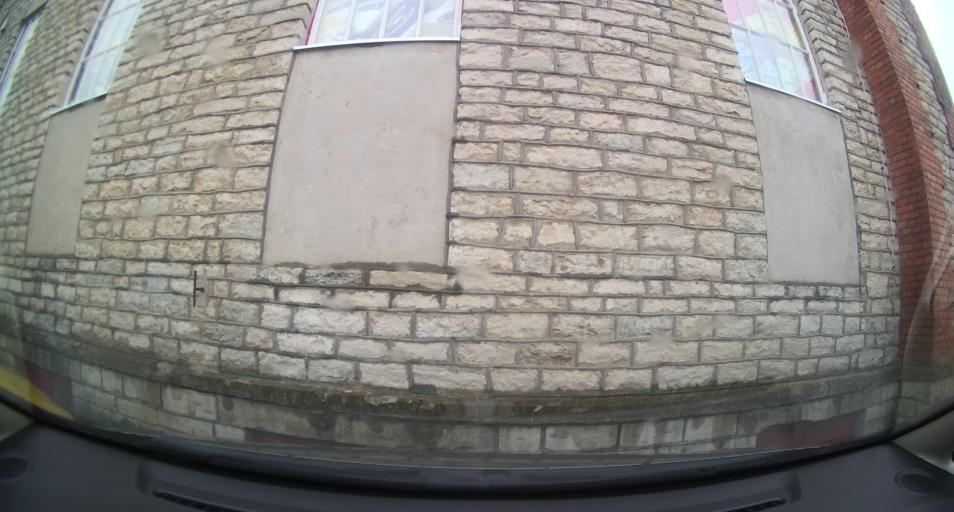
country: EE
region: Harju
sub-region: Nissi vald
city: Turba
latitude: 59.0783
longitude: 24.2423
